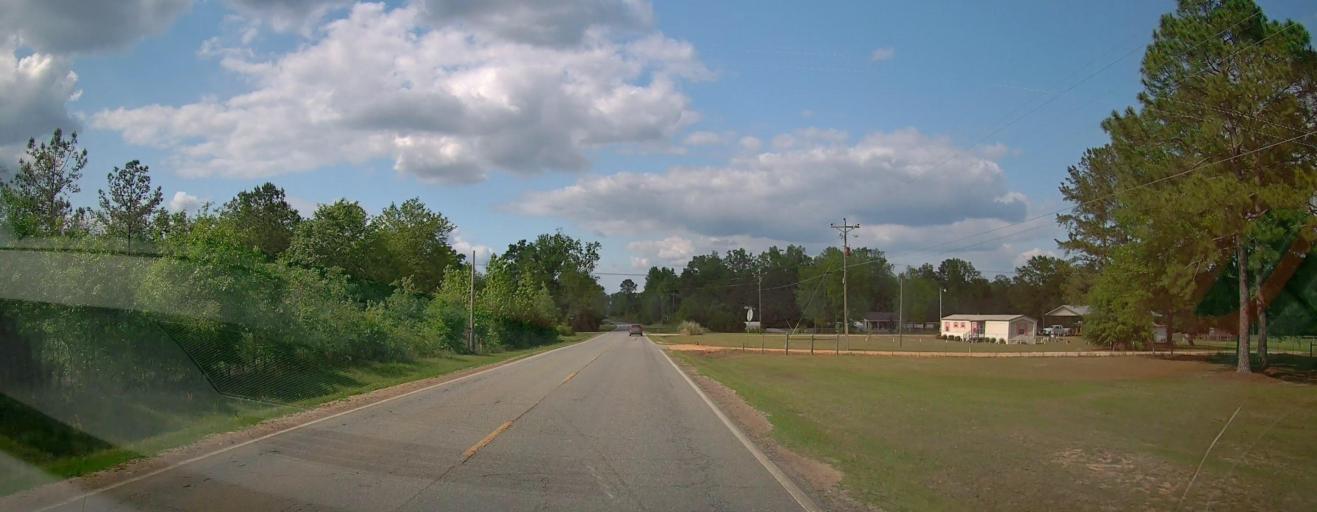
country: US
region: Georgia
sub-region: Laurens County
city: East Dublin
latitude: 32.5936
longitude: -82.8654
